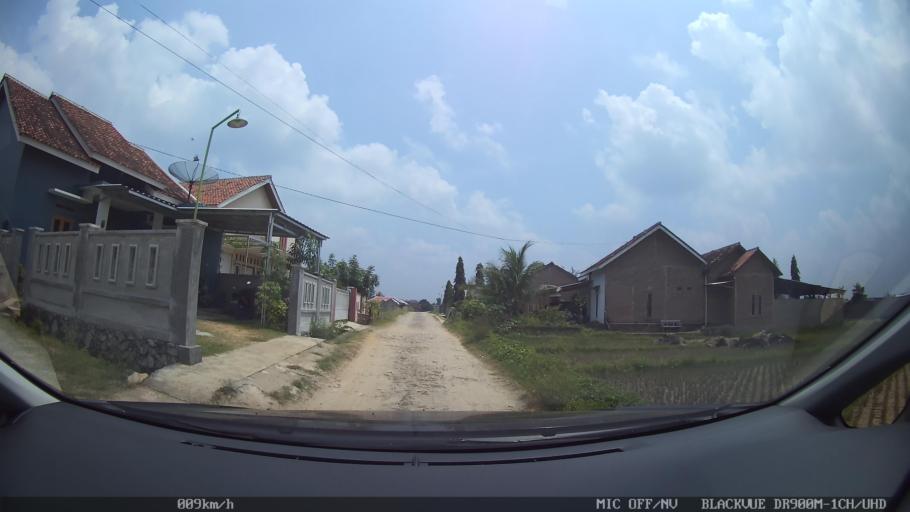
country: ID
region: Lampung
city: Pringsewu
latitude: -5.3526
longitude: 104.9888
